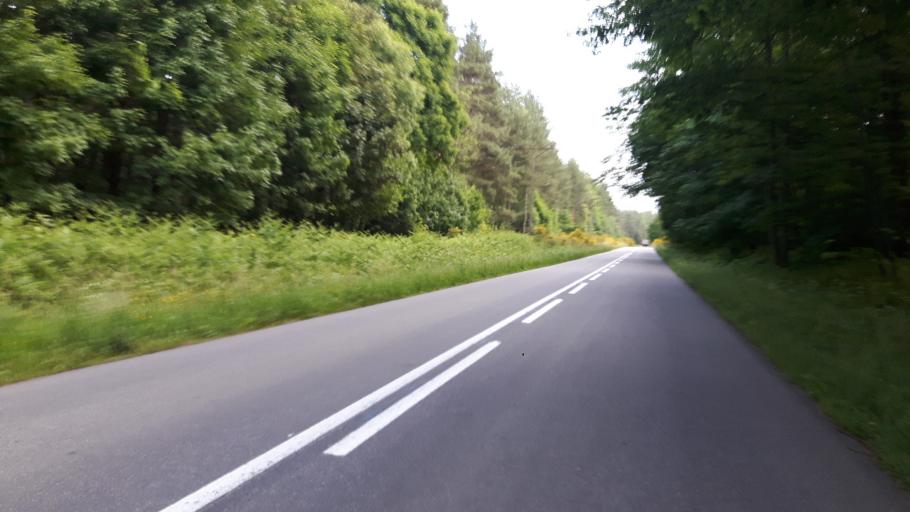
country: PL
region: Pomeranian Voivodeship
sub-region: Powiat leborski
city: Leba
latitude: 54.7460
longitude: 17.7203
